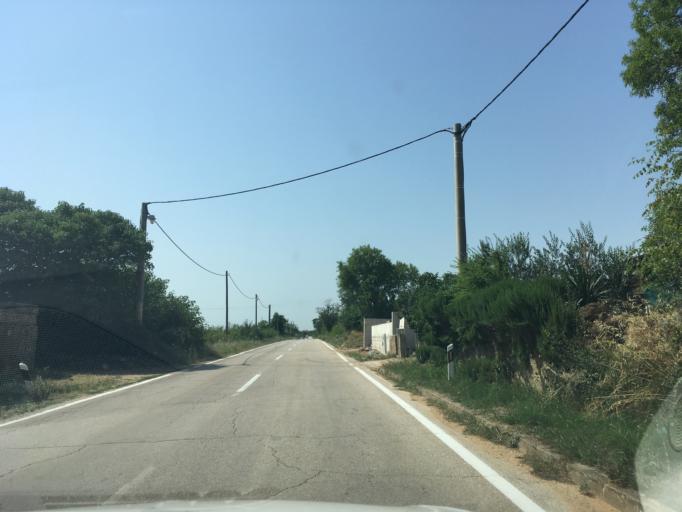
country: HR
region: Zadarska
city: Benkovac
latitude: 44.0208
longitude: 15.6378
